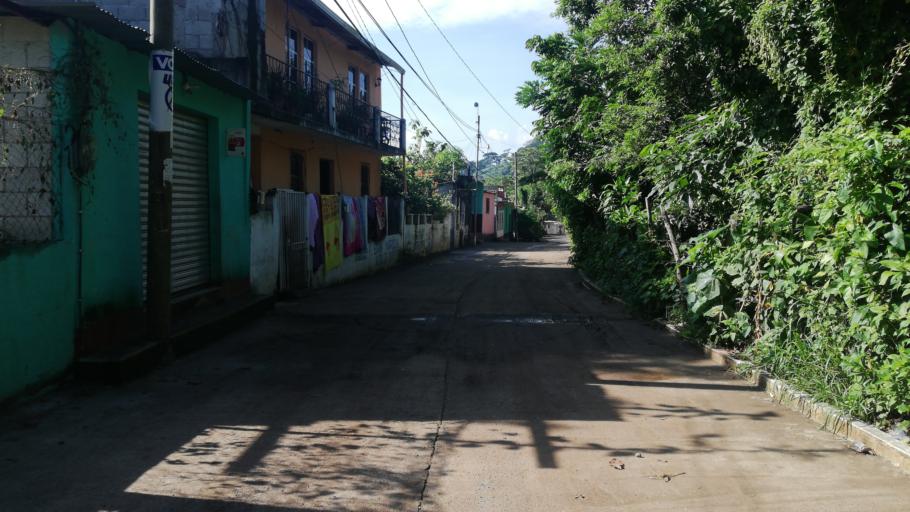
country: GT
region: Santa Rosa
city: Cuilapa
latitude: 14.2819
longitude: -90.3028
